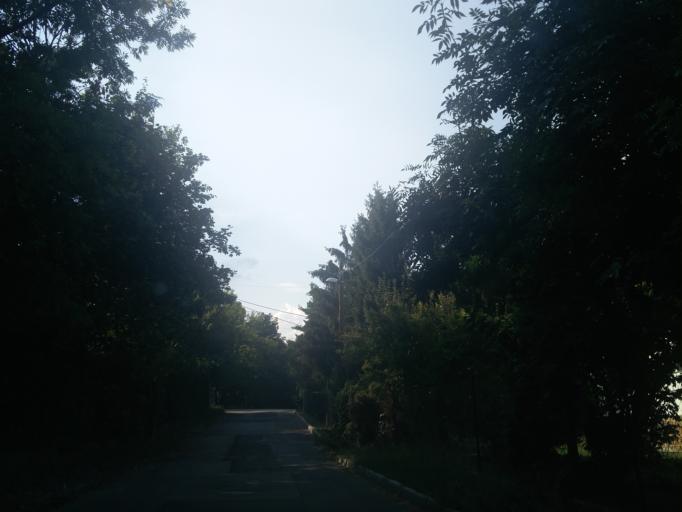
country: HU
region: Budapest
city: Budapest XII. keruelet
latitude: 47.4965
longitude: 18.9794
